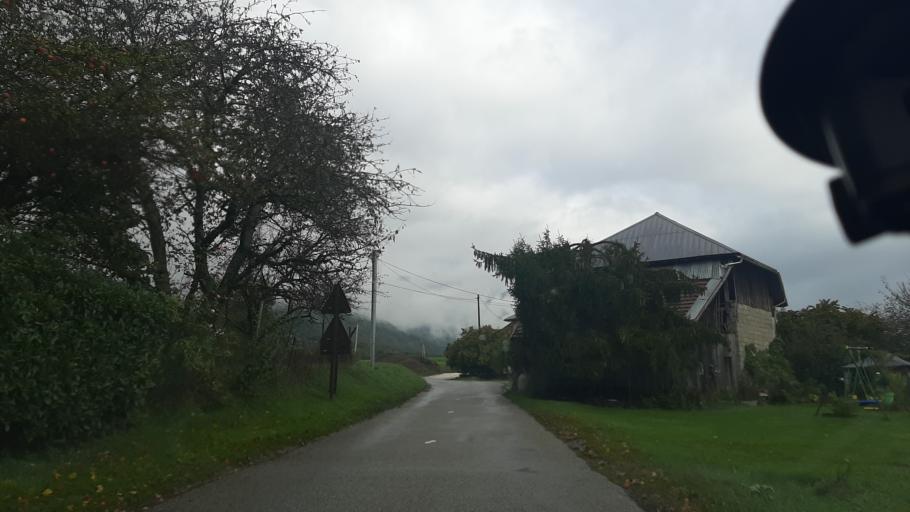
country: FR
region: Rhone-Alpes
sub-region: Departement de la Savoie
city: Sainte-Helene-sur-Isere
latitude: 45.6150
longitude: 6.2870
